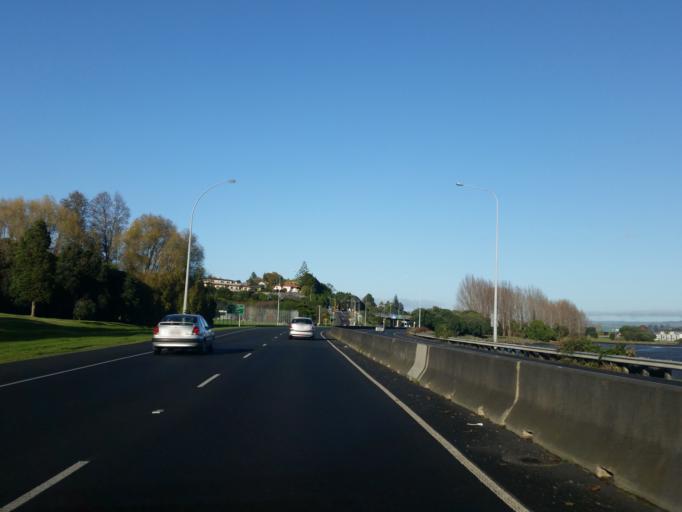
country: NZ
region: Bay of Plenty
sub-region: Tauranga City
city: Tauranga
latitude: -37.6934
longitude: 176.1567
